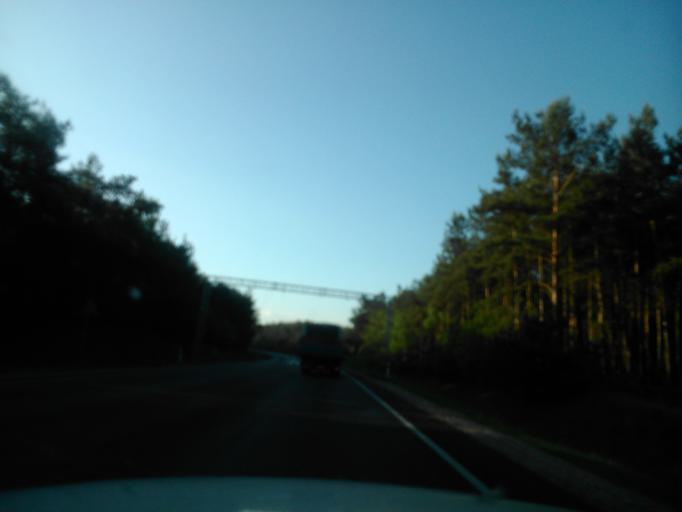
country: PL
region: Masovian Voivodeship
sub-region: Powiat plocki
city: Wyszogrod
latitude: 52.3653
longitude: 20.1935
